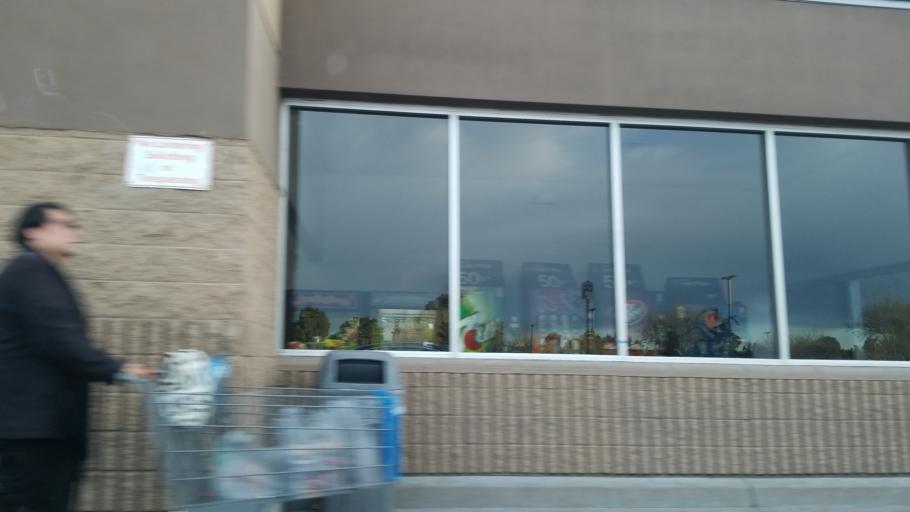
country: US
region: Arizona
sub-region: Maricopa County
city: Phoenix
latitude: 33.5225
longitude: -112.0926
